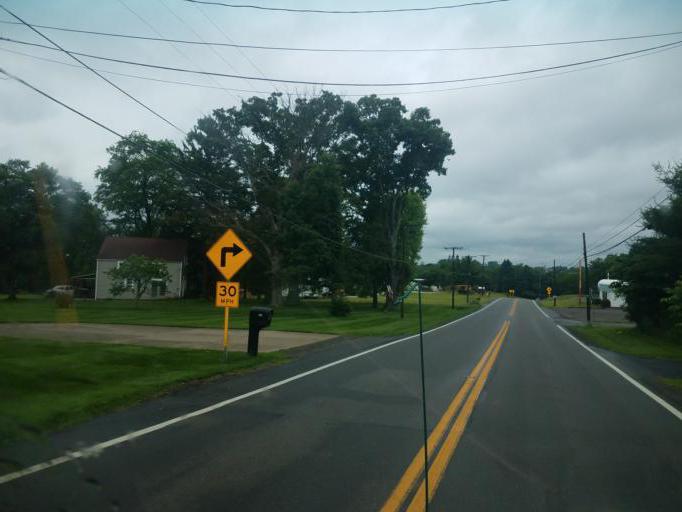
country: US
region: Ohio
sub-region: Carroll County
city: Carrollton
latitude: 40.5678
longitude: -81.0742
